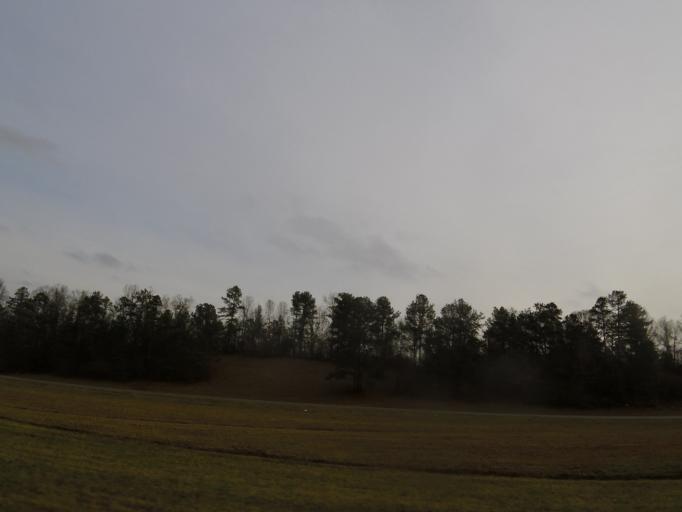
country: US
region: Alabama
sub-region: Autauga County
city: Prattville
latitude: 32.5115
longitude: -86.4271
